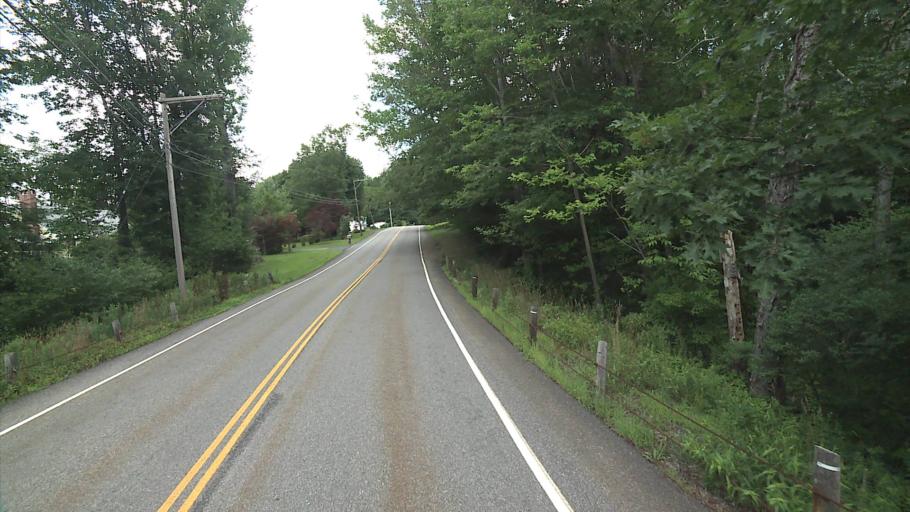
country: US
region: Connecticut
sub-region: Litchfield County
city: Winsted
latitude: 41.9992
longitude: -72.9795
